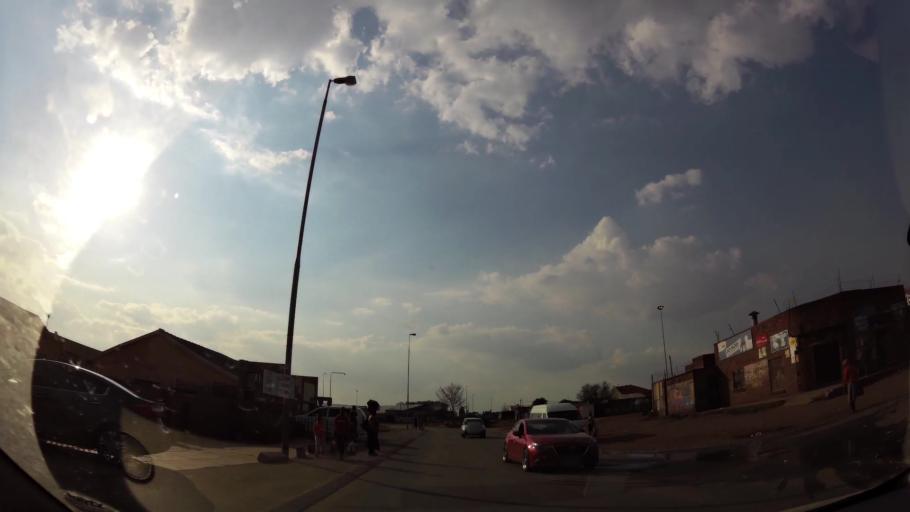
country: ZA
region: Gauteng
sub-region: Ekurhuleni Metropolitan Municipality
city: Germiston
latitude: -26.3588
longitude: 28.2076
